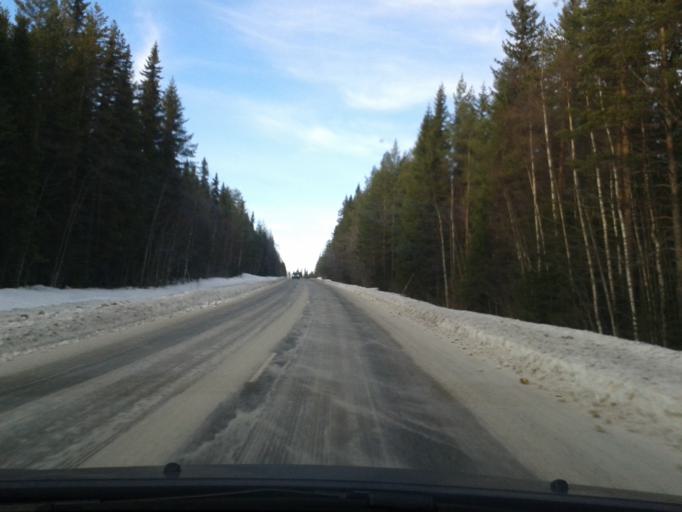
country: SE
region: Vaesternorrland
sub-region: OErnskoeldsviks Kommun
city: Bredbyn
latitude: 63.5885
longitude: 17.9223
